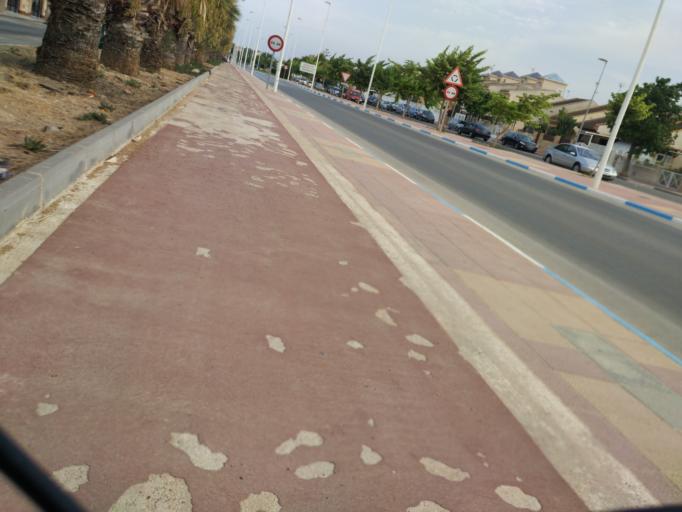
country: ES
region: Murcia
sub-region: Murcia
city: Los Alcazares
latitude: 37.7488
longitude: -0.8550
